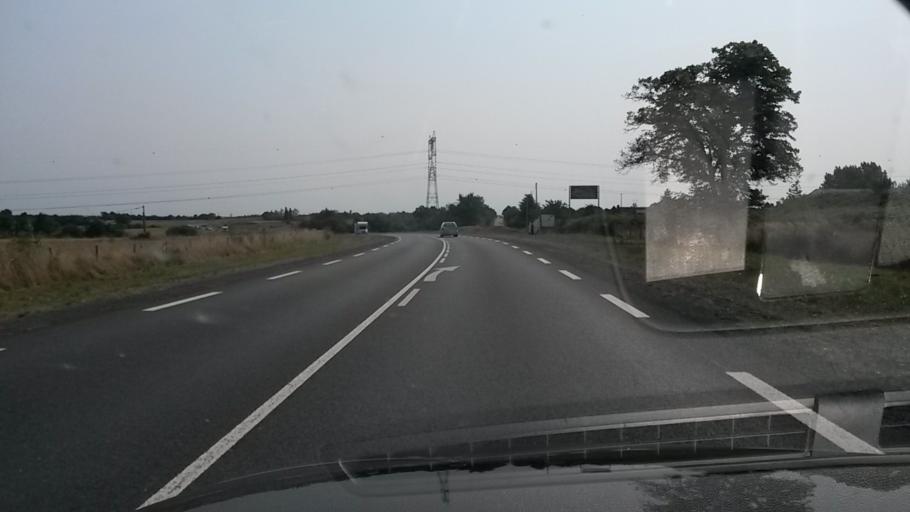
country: FR
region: Pays de la Loire
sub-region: Departement de la Loire-Atlantique
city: Mesanger
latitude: 47.4261
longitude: -1.1871
